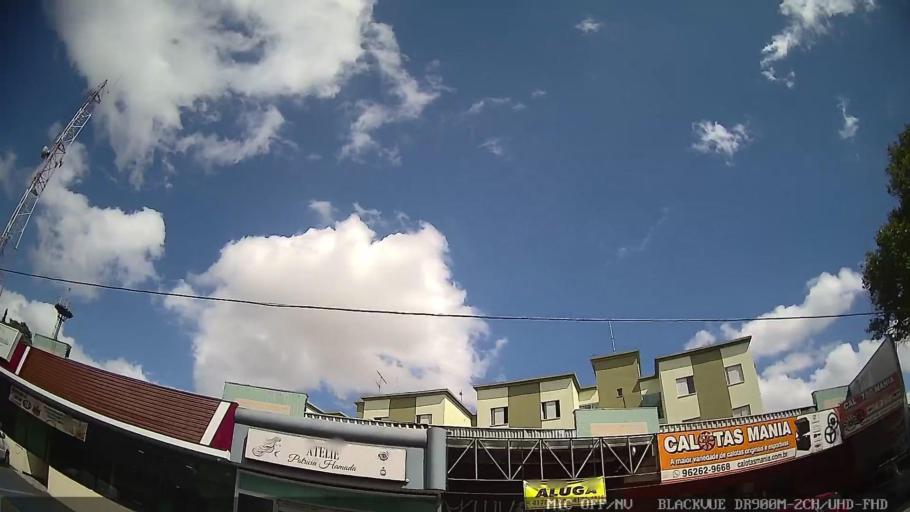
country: BR
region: Sao Paulo
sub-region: Diadema
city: Diadema
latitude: -23.6543
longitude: -46.5931
